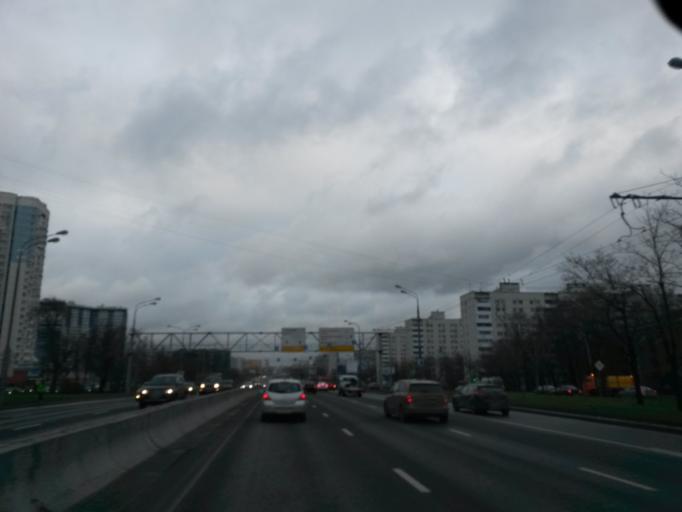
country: RU
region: Moscow
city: Chertanovo Yuzhnoye
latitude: 55.5913
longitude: 37.6003
